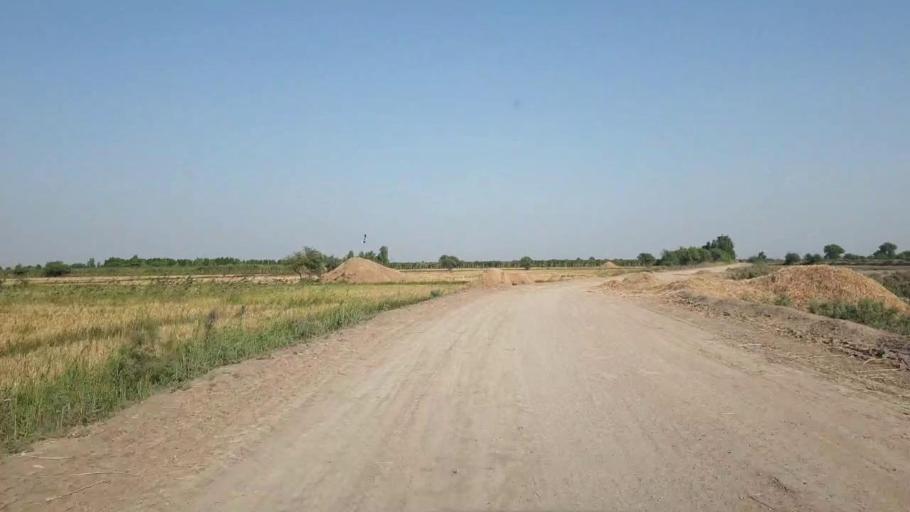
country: PK
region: Sindh
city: Rajo Khanani
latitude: 25.0092
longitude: 68.7743
